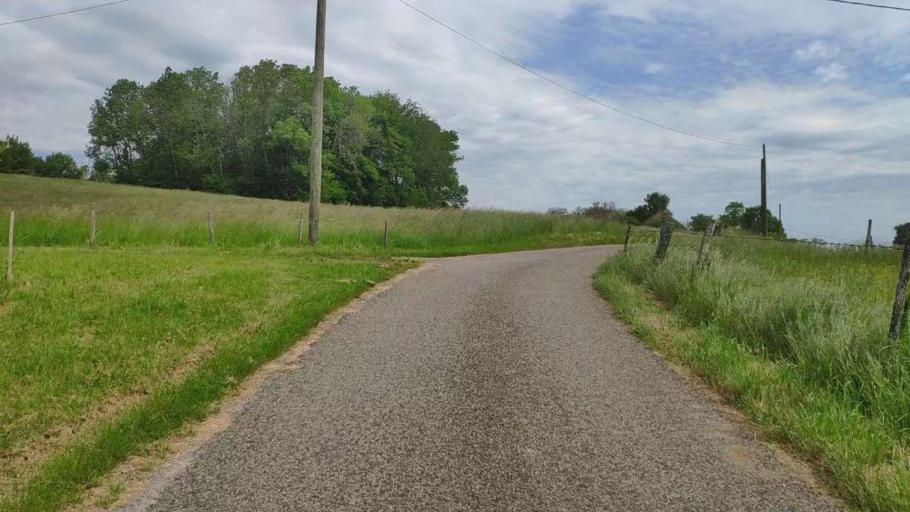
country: FR
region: Franche-Comte
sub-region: Departement du Jura
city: Poligny
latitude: 46.7904
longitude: 5.6422
